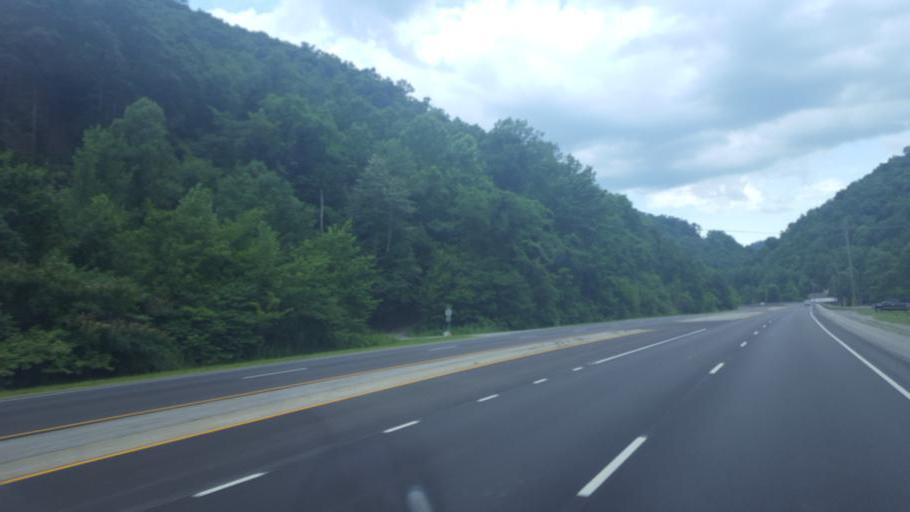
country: US
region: Kentucky
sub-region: Pike County
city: Pikeville
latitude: 37.3298
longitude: -82.5589
